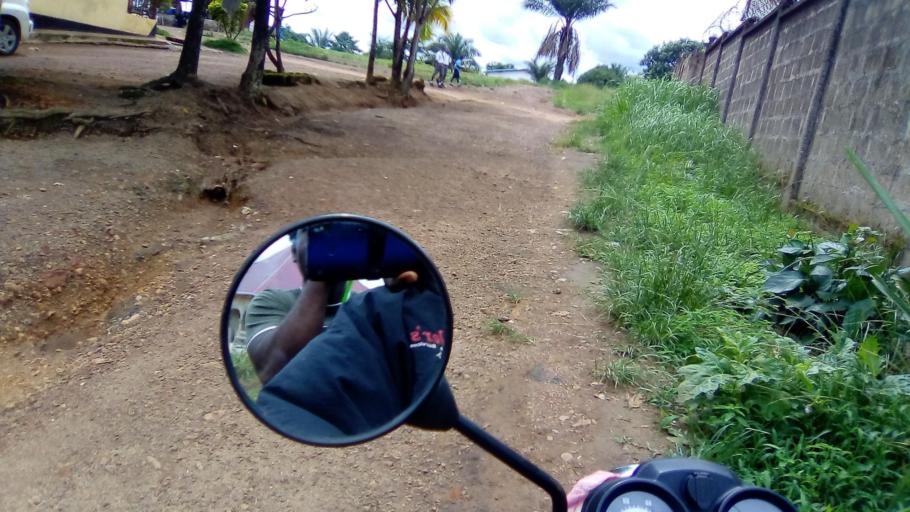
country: SL
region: Southern Province
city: Bo
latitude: 7.9325
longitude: -11.7206
